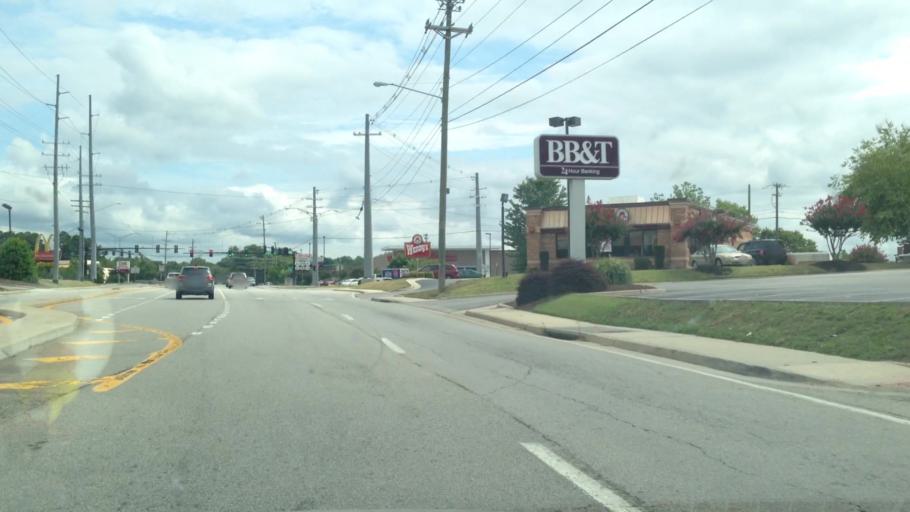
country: US
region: Virginia
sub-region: City of Danville
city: Danville
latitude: 36.6319
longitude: -79.3954
